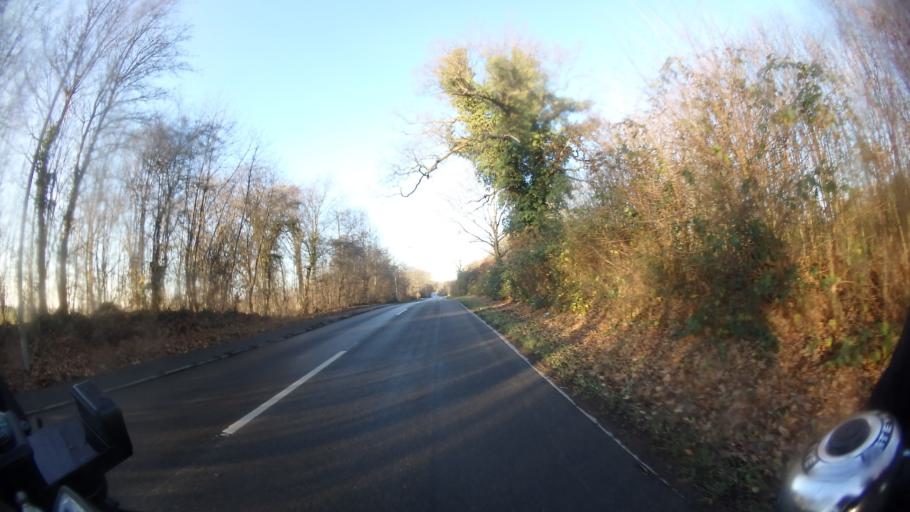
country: DE
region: Schleswig-Holstein
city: Travemuende
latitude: 53.9763
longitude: 10.8664
